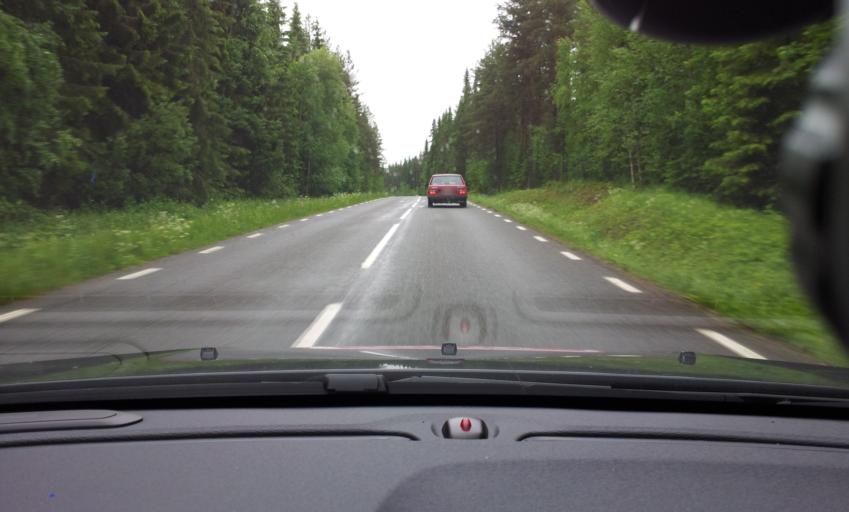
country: SE
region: Jaemtland
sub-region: Stroemsunds Kommun
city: Stroemsund
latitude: 63.4623
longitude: 15.4567
